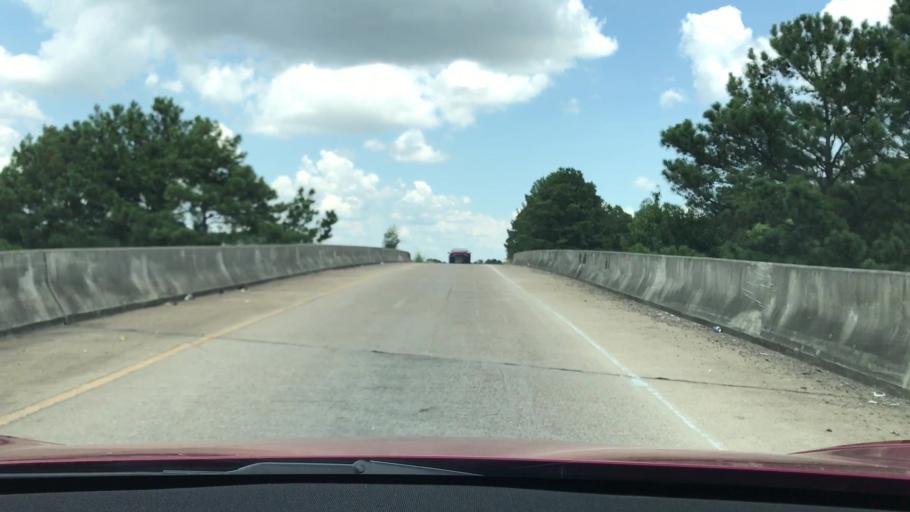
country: US
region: Louisiana
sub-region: Bossier Parish
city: Bossier City
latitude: 32.4147
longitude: -93.7889
